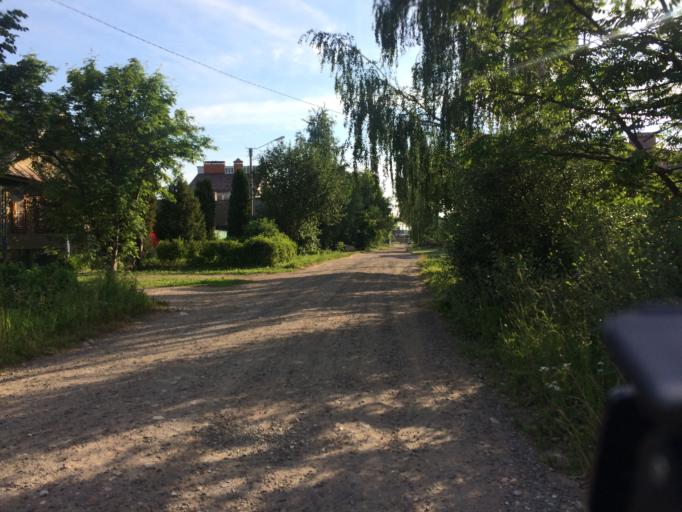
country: RU
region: Mariy-El
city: Yoshkar-Ola
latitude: 56.6487
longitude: 47.9152
